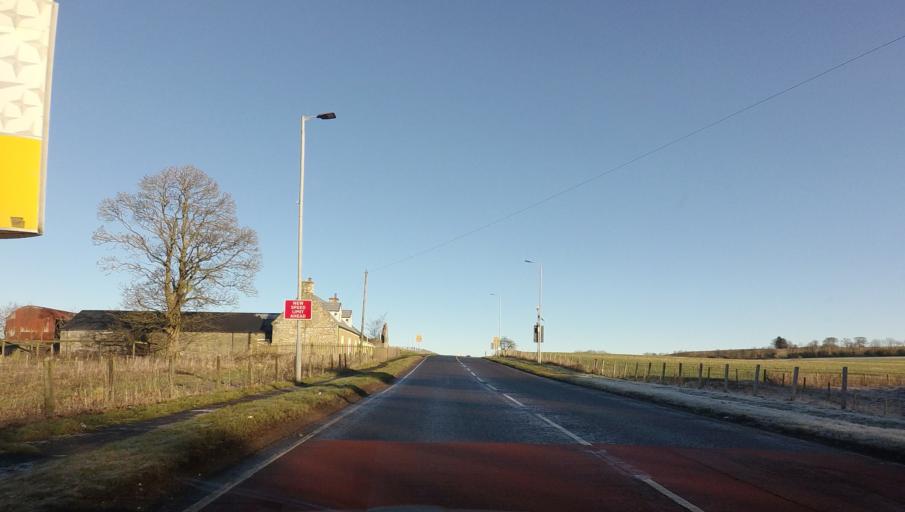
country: GB
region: Scotland
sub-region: North Lanarkshire
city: Shotts
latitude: 55.8025
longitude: -3.8248
